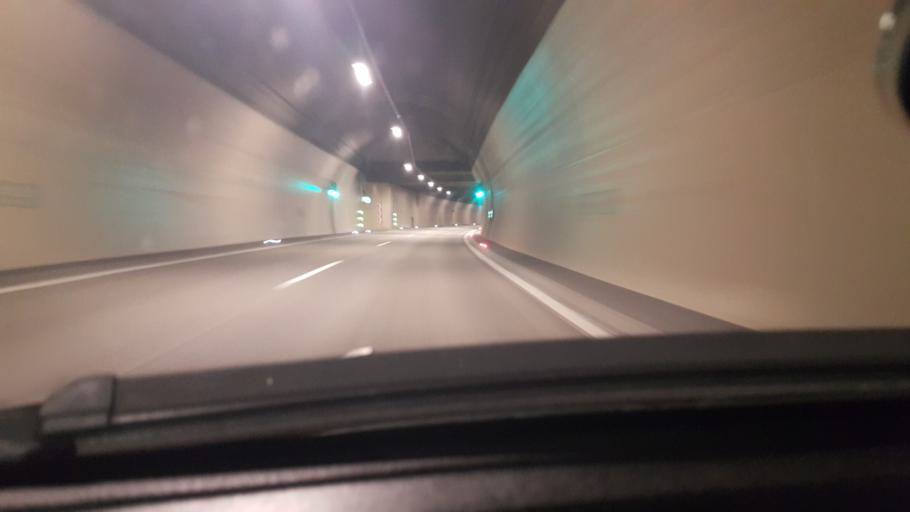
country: AT
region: Carinthia
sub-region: Klagenfurt am Woerthersee
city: Klagenfurt am Woerthersee
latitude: 46.6567
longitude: 14.2964
